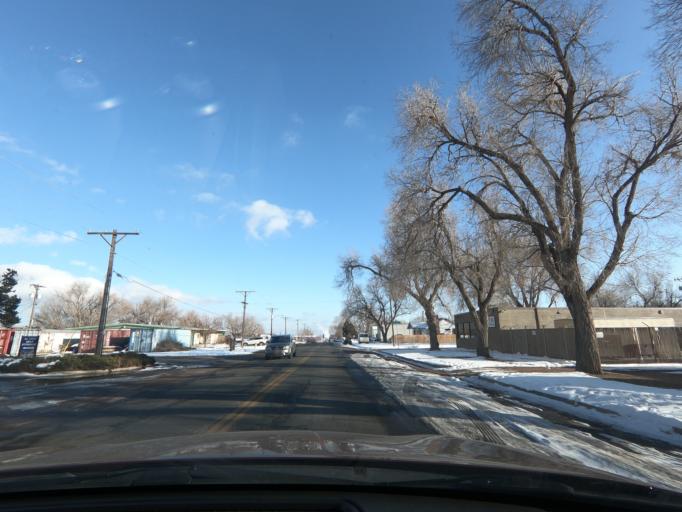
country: US
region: Colorado
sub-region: El Paso County
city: Colorado Springs
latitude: 38.8407
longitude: -104.8627
